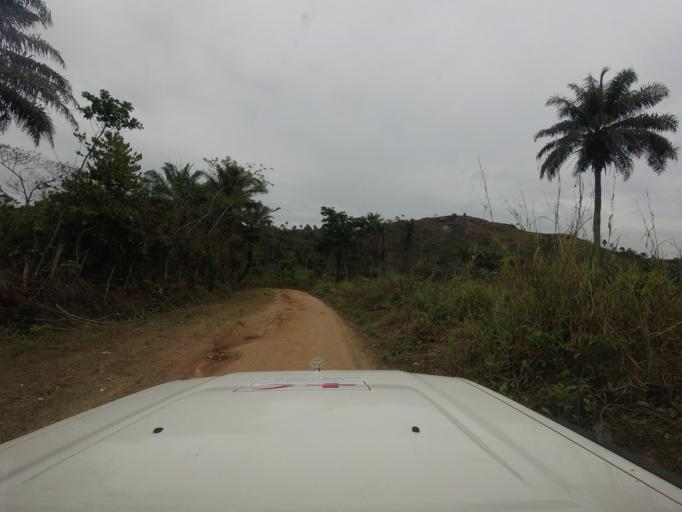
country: SL
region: Eastern Province
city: Buedu
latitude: 8.2741
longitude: -10.2769
